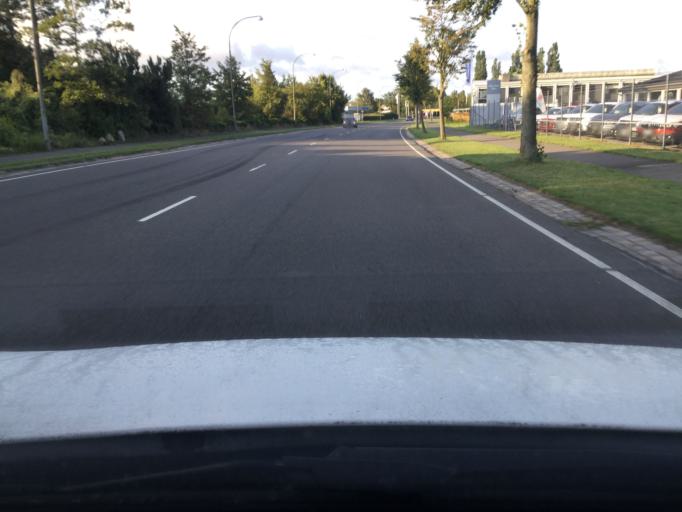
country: DK
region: Zealand
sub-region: Lolland Kommune
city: Nakskov
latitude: 54.8283
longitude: 11.1622
